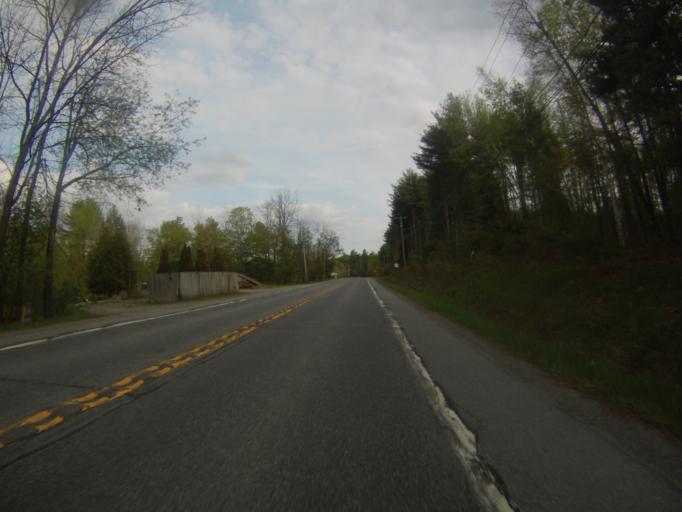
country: US
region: New York
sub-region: Warren County
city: Warrensburg
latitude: 43.6567
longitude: -73.9510
